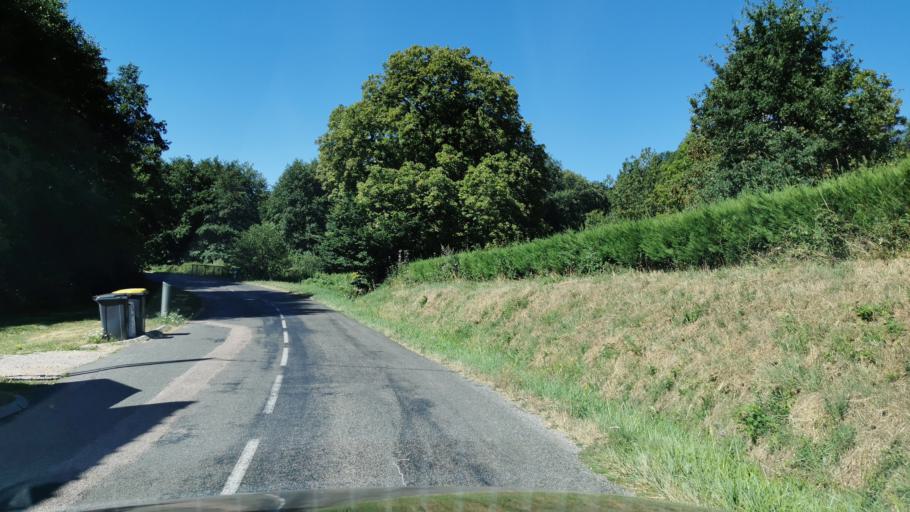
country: FR
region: Bourgogne
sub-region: Departement de Saone-et-Loire
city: Le Breuil
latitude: 46.7933
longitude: 4.4835
